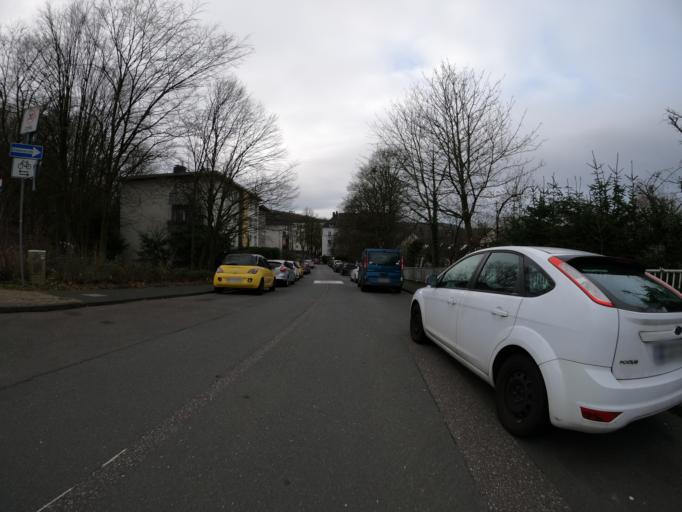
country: DE
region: North Rhine-Westphalia
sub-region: Regierungsbezirk Dusseldorf
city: Wuppertal
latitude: 51.2480
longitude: 7.1468
